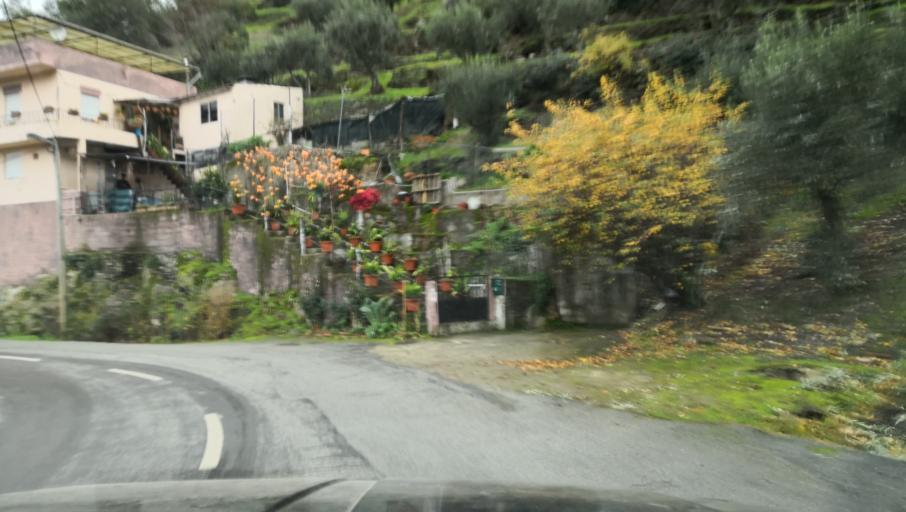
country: PT
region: Vila Real
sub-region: Santa Marta de Penaguiao
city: Santa Marta de Penaguiao
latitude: 41.2228
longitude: -7.7487
